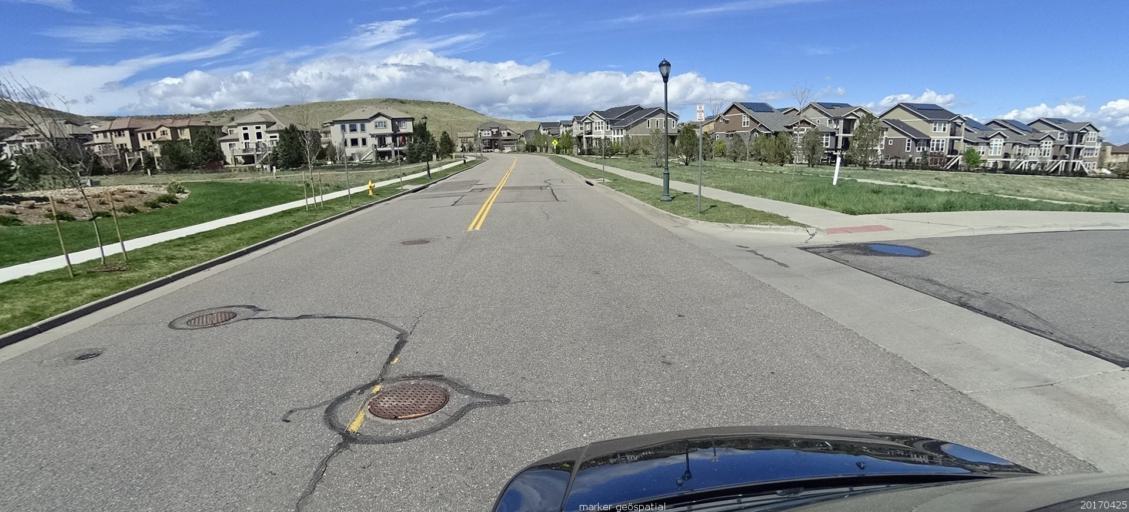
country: US
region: Colorado
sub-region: Douglas County
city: Carriage Club
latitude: 39.5267
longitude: -104.8811
